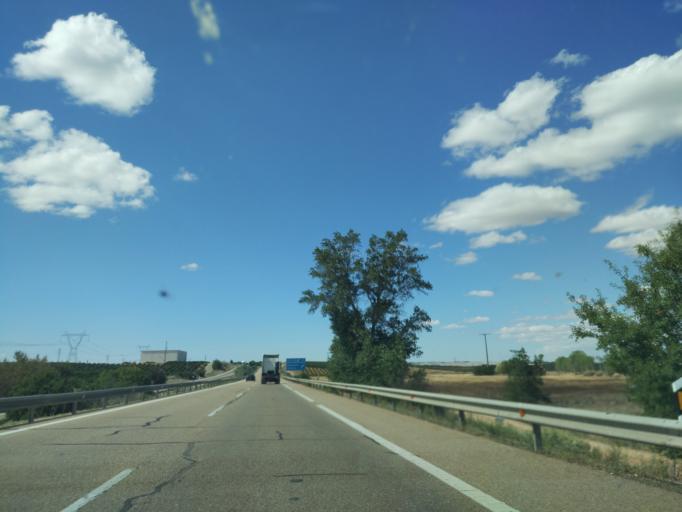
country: ES
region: Castille and Leon
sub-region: Provincia de Valladolid
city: Rueda
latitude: 41.4340
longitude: -4.9727
